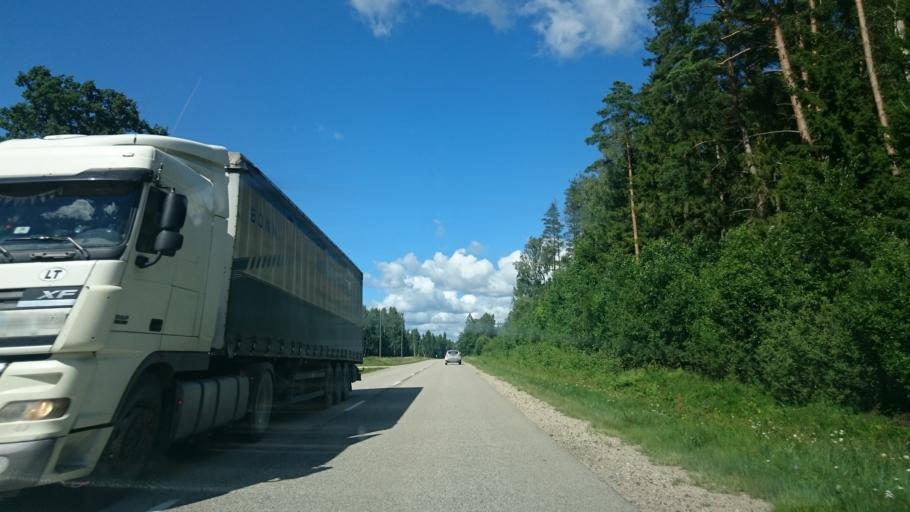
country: LV
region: Kuldigas Rajons
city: Kuldiga
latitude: 56.8823
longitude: 21.8774
